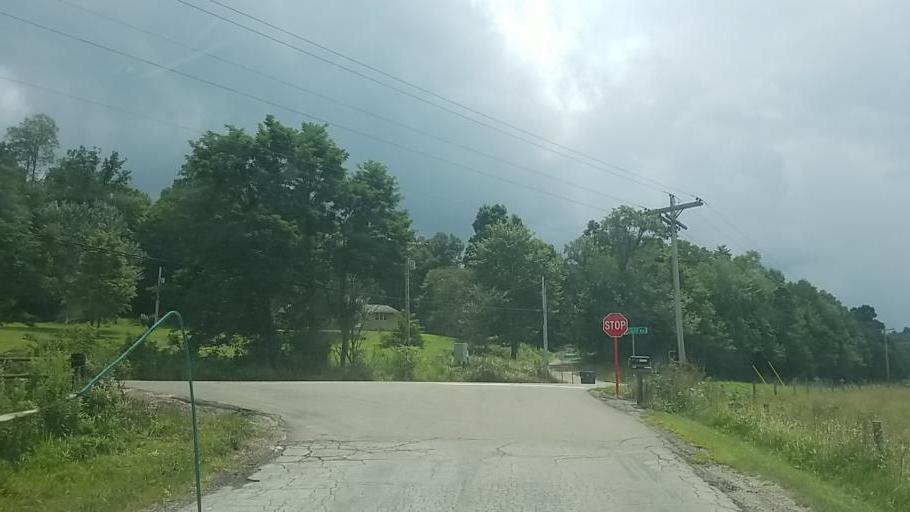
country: US
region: Ohio
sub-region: Muskingum County
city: Frazeysburg
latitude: 40.1967
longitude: -82.2625
